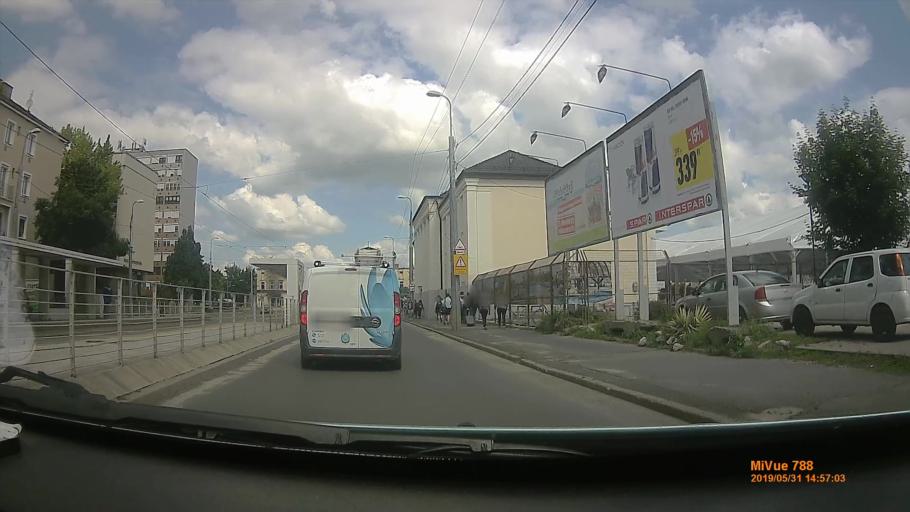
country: HU
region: Borsod-Abauj-Zemplen
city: Miskolc
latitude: 48.1026
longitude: 20.8065
